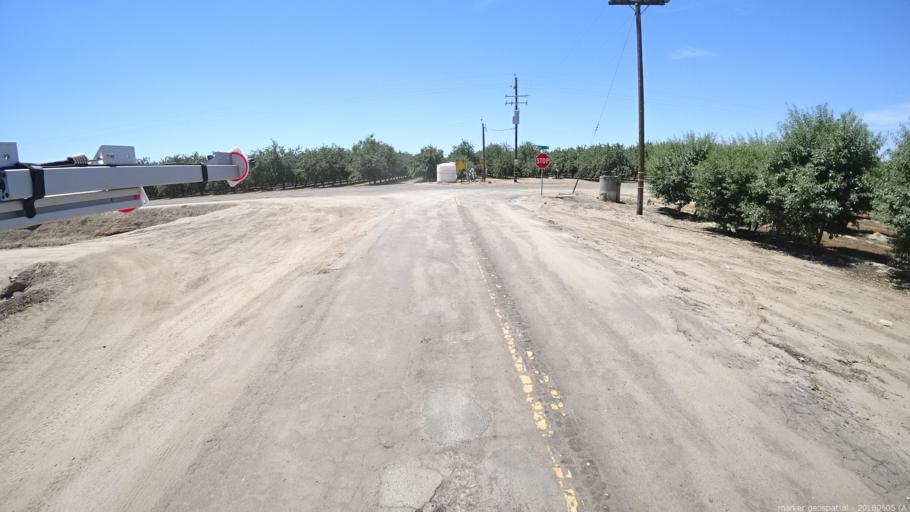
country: US
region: California
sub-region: Madera County
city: Chowchilla
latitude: 37.0548
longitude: -120.4192
